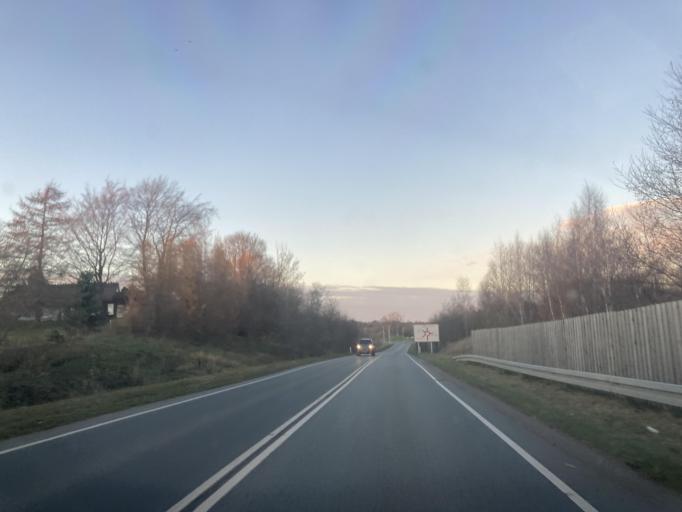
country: DK
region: Capital Region
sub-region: Gribskov Kommune
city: Graested
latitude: 56.0578
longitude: 12.2749
